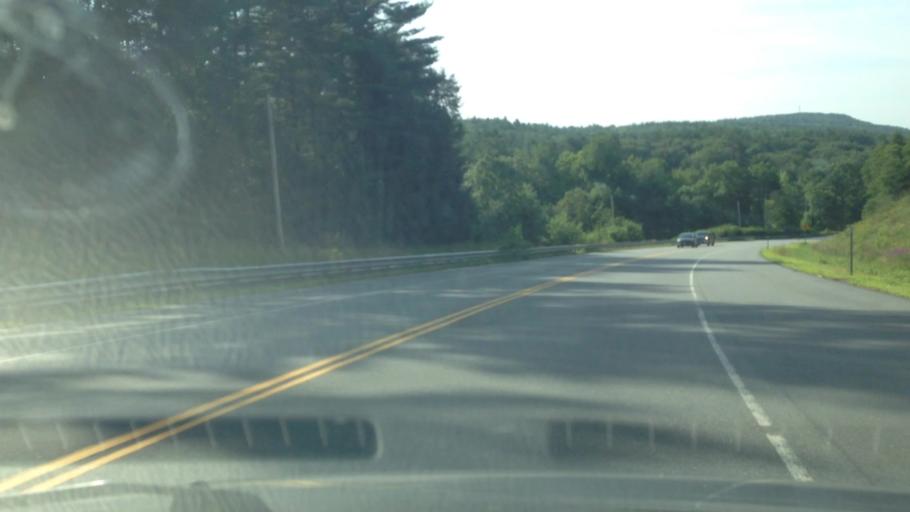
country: US
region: New Hampshire
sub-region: Cheshire County
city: Keene
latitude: 42.9540
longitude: -72.2707
